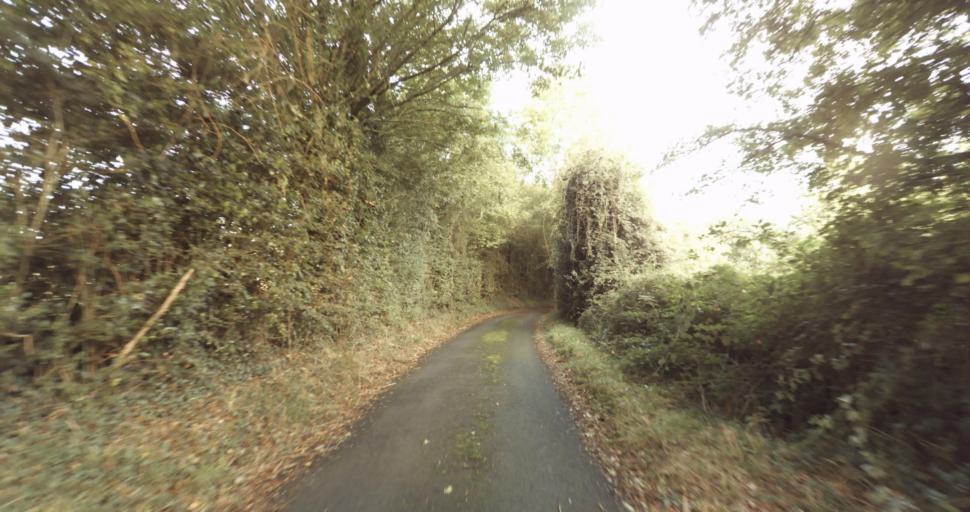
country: FR
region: Lower Normandy
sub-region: Departement de l'Orne
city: Vimoutiers
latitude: 48.8881
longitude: 0.2251
